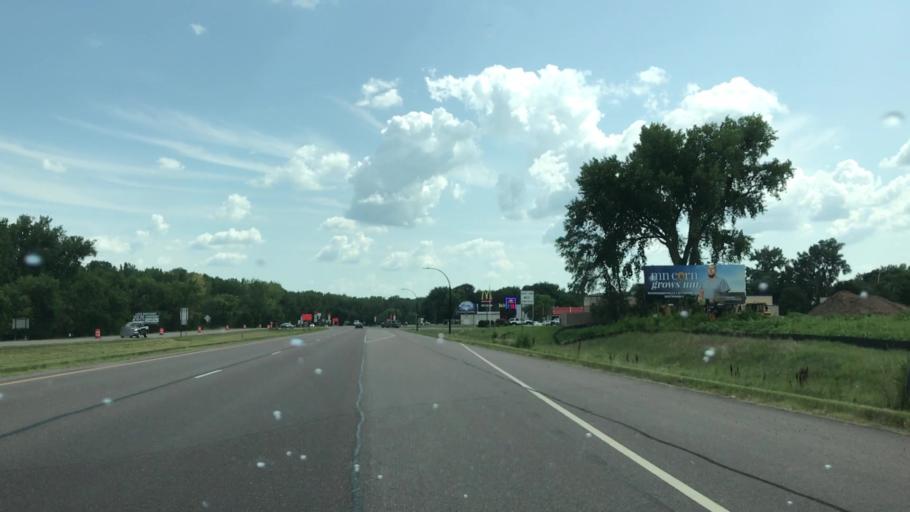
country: US
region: Minnesota
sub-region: Nicollet County
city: Saint Peter
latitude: 44.3417
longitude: -93.9492
